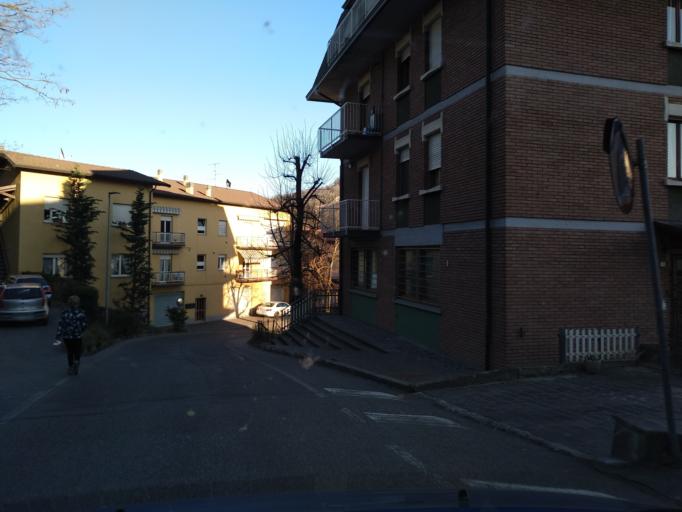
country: IT
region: Emilia-Romagna
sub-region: Provincia di Reggio Emilia
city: Castelnovo ne'Monti
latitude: 44.4331
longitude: 10.4010
